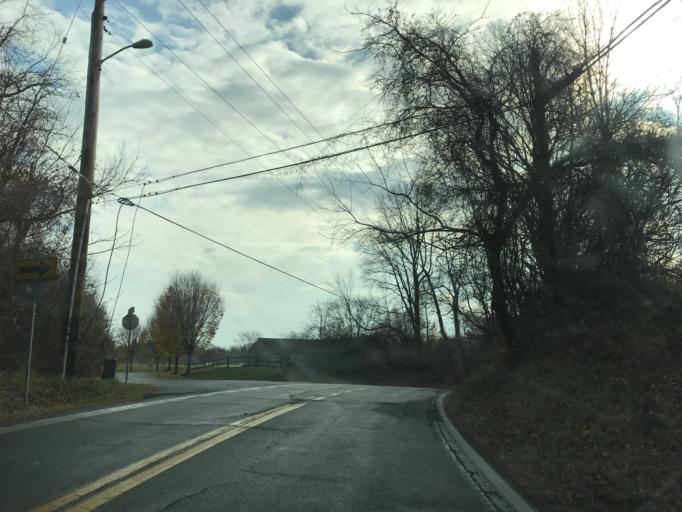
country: US
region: Maryland
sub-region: Baltimore County
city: Hunt Valley
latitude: 39.5705
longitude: -76.5950
